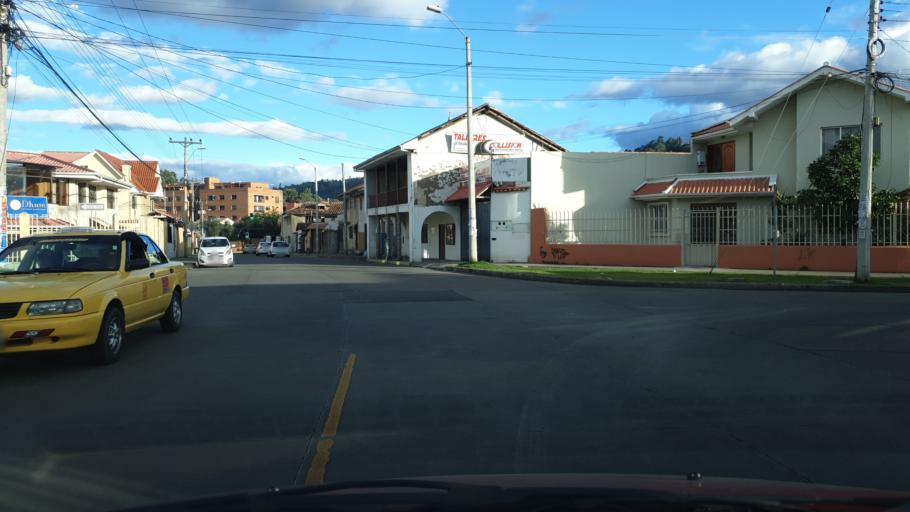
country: EC
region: Azuay
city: Cuenca
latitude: -2.9120
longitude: -79.0163
